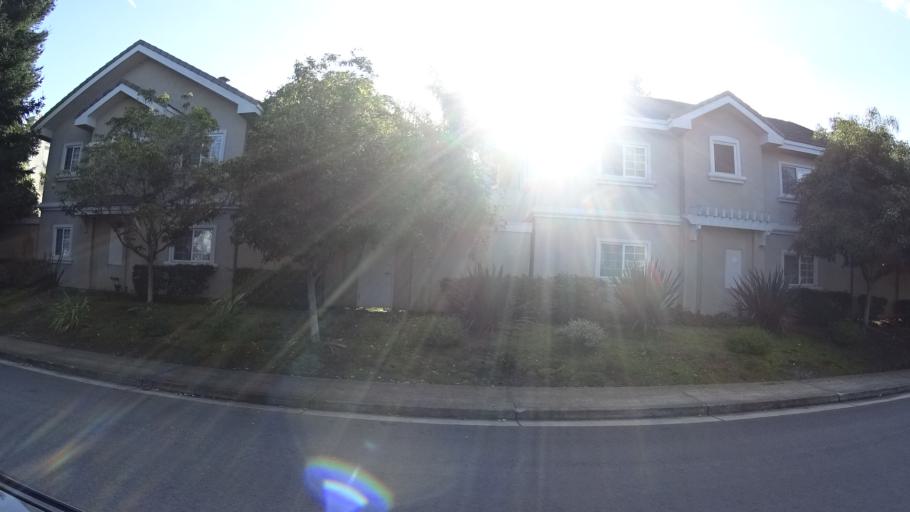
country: US
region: California
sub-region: Santa Clara County
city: Sunnyvale
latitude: 37.3717
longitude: -122.0427
